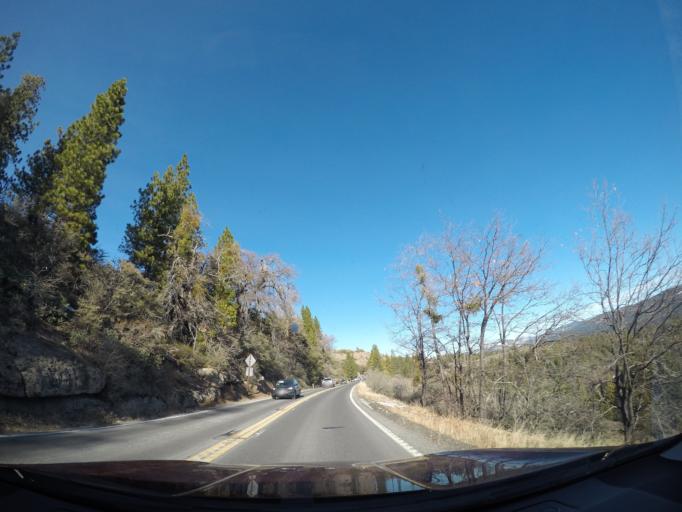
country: US
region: California
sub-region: Tuolumne County
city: Twain Harte
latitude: 38.1388
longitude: -120.0905
